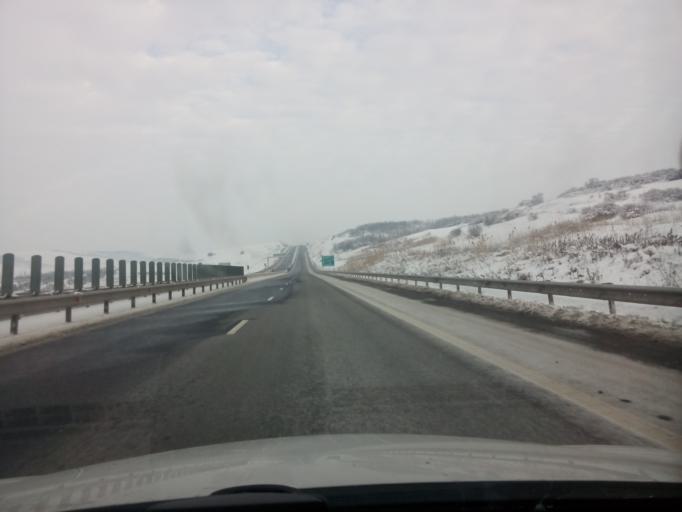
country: RO
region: Alba
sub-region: Comuna Cut
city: Cut
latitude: 45.9226
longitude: 23.6711
